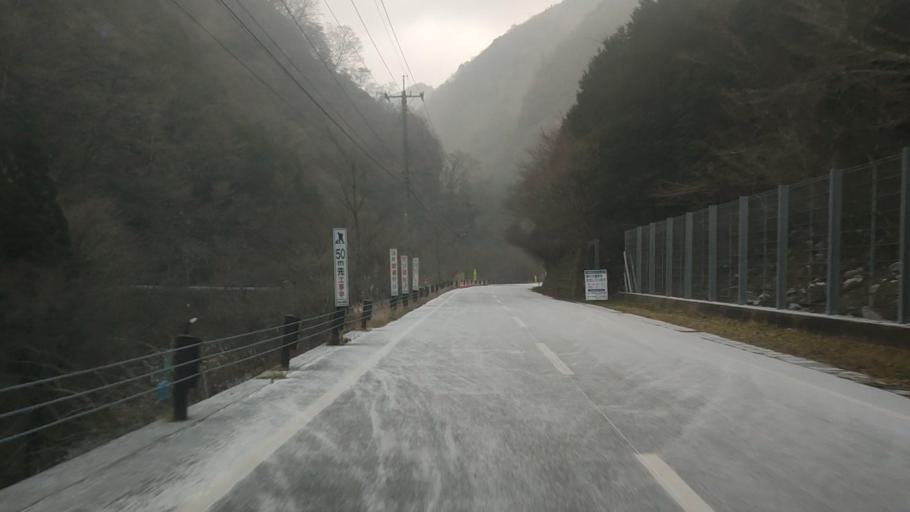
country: JP
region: Kumamoto
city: Matsubase
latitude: 32.5571
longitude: 130.9206
